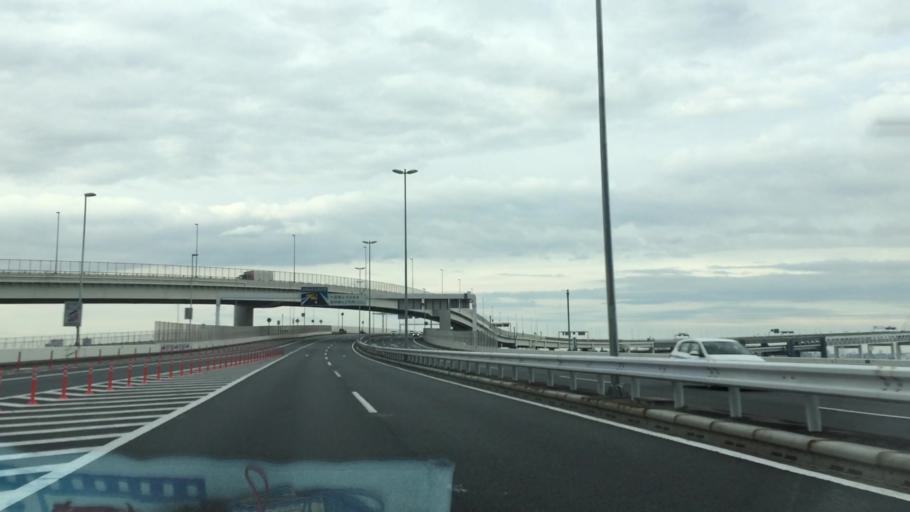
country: JP
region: Kanagawa
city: Yokohama
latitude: 35.4375
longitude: 139.6684
